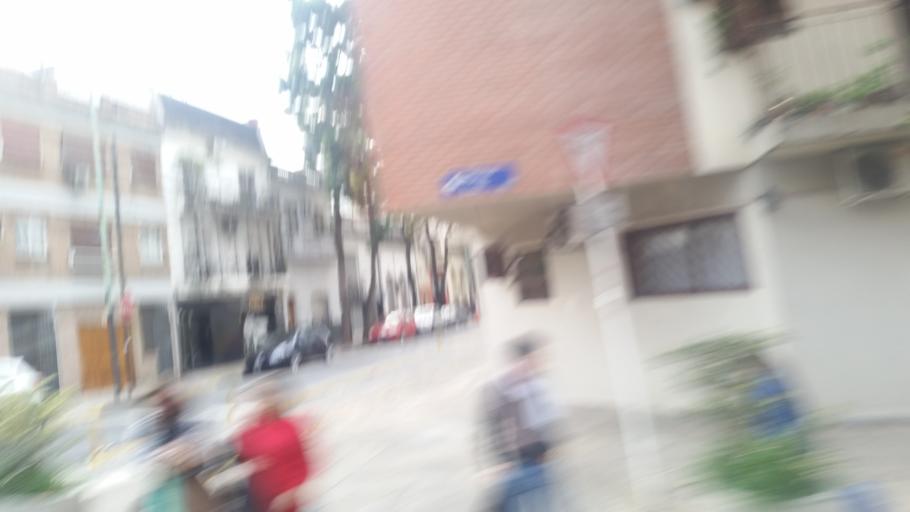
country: AR
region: Buenos Aires F.D.
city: Colegiales
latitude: -34.6072
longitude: -58.4227
